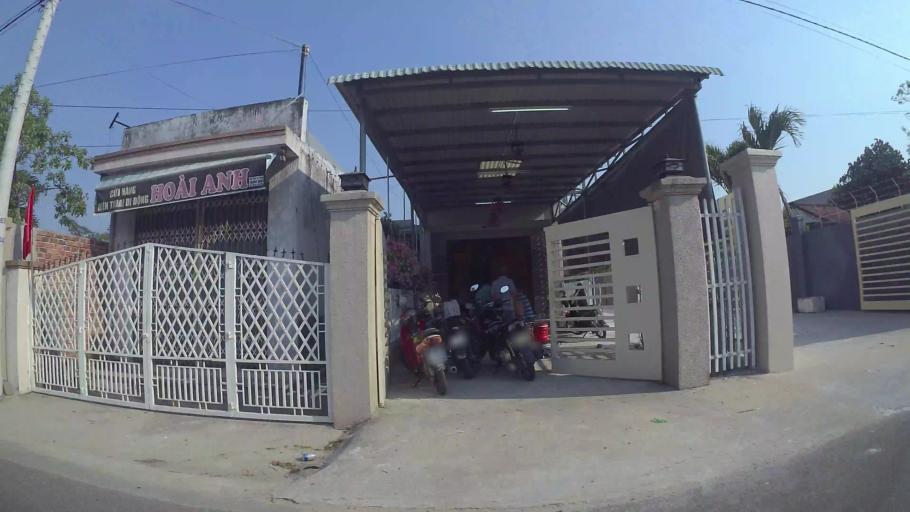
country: VN
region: Quang Nam
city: Quang Nam
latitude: 15.9456
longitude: 108.2599
